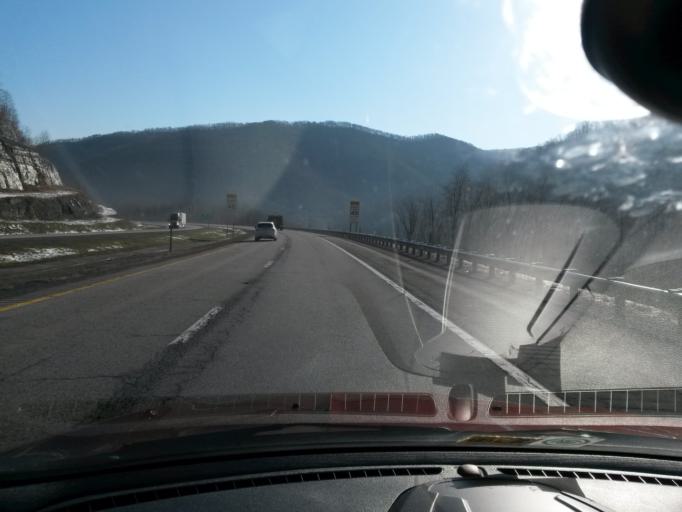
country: US
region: West Virginia
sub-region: Nicholas County
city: Craigsville
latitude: 38.4801
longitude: -80.7659
